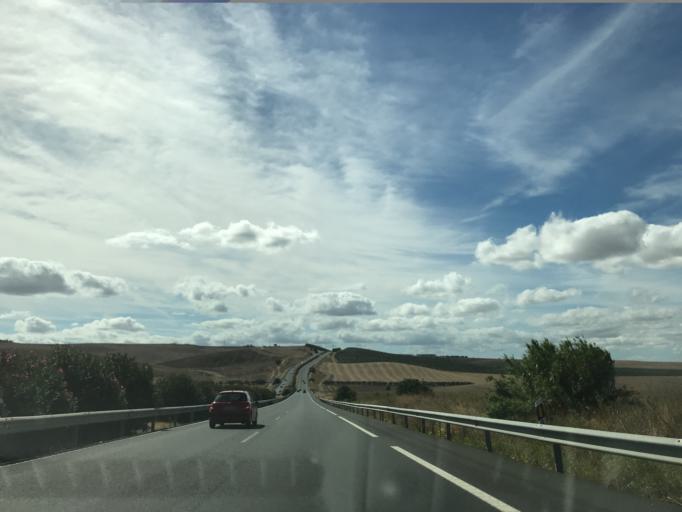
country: ES
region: Andalusia
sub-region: Province of Cordoba
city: La Victoria
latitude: 37.7371
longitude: -4.8506
